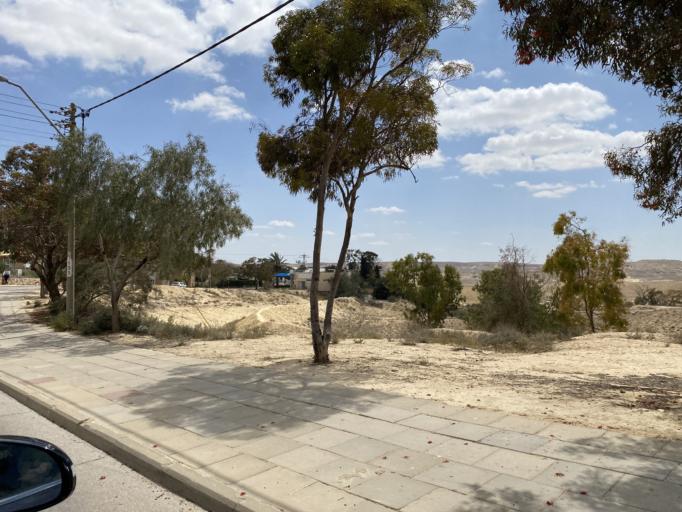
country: IL
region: Southern District
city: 'Arad
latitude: 31.2555
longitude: 35.2144
